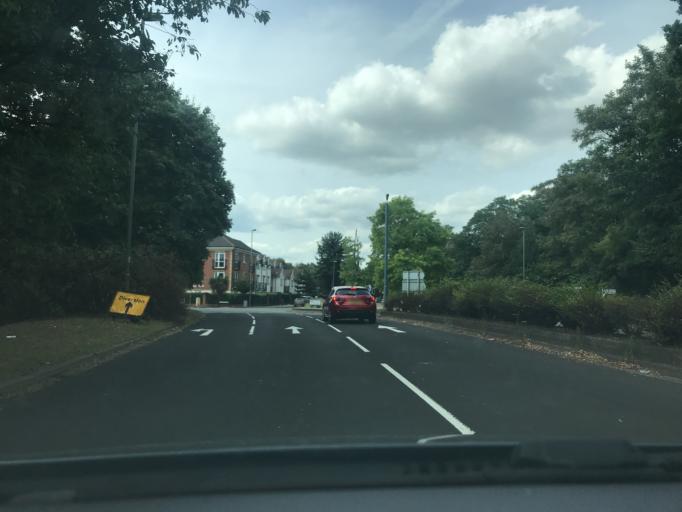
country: GB
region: England
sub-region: Surrey
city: Addlestone
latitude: 51.3746
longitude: -0.4789
